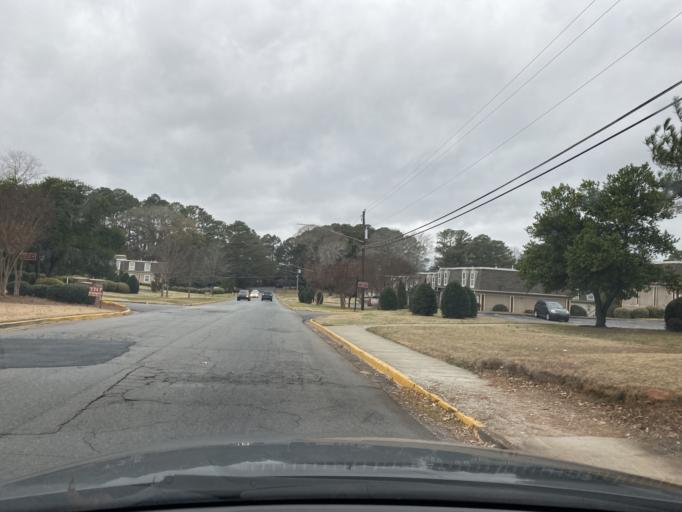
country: US
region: Georgia
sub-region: DeKalb County
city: Pine Mountain
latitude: 33.7013
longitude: -84.1444
